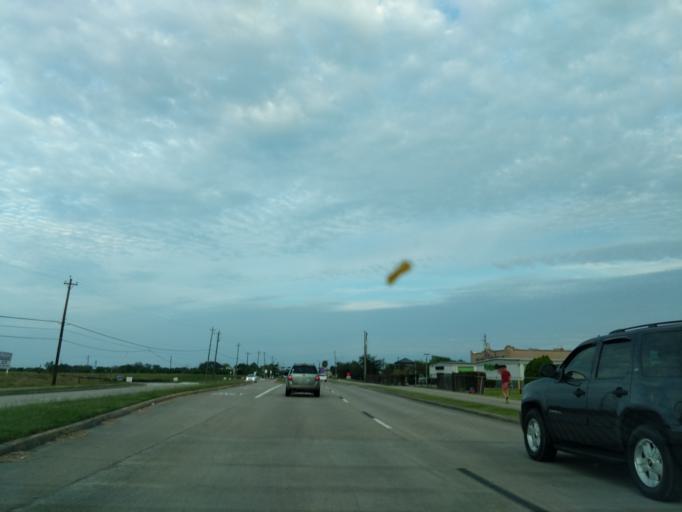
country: US
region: Texas
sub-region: Galveston County
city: Clear Lake Shores
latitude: 29.5289
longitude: -95.0368
